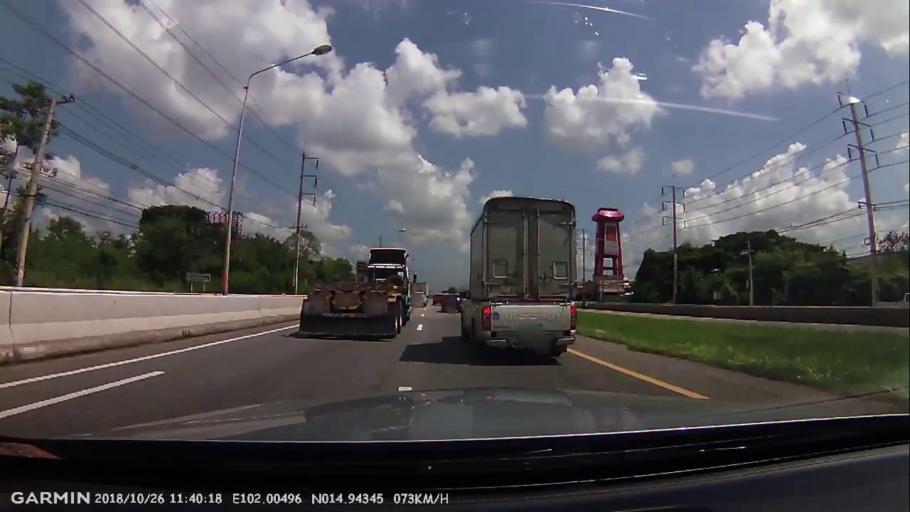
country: TH
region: Nakhon Ratchasima
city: Kham Thale So
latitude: 14.9435
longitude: 102.0051
